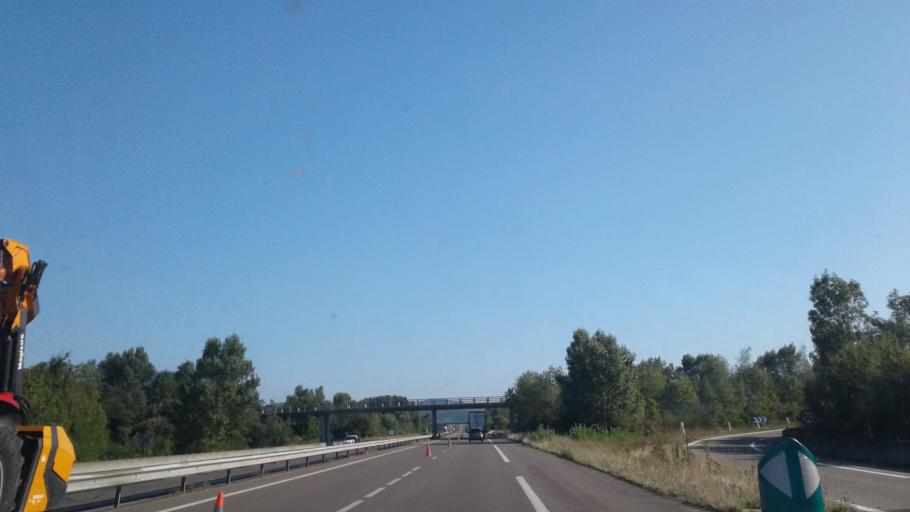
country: FR
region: Rhone-Alpes
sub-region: Departement de l'Ain
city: Ambronay
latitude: 46.0439
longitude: 5.3246
